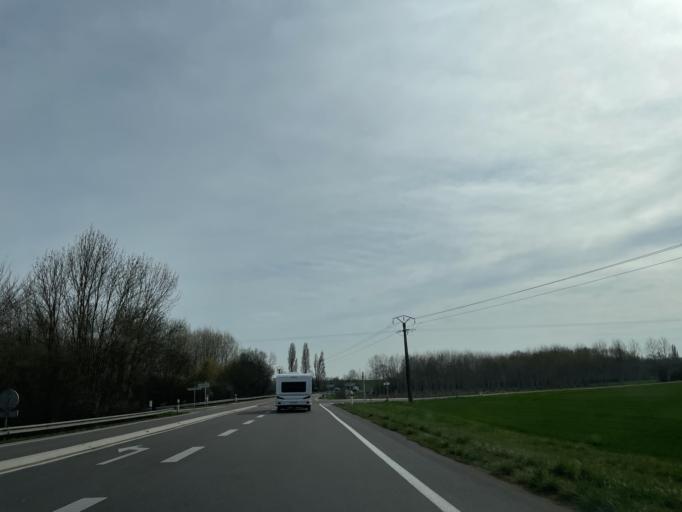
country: FR
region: Champagne-Ardenne
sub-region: Departement de l'Aube
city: Romilly-sur-Seine
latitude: 48.5128
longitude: 3.6801
